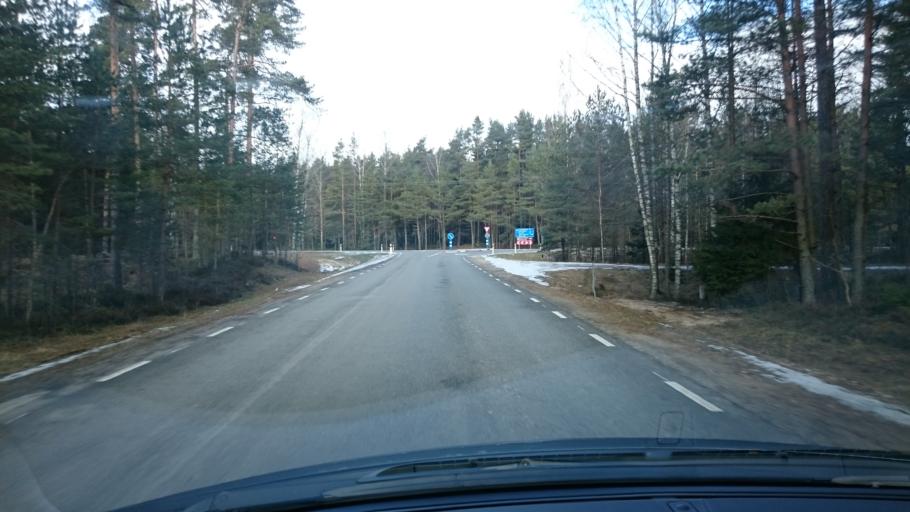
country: EE
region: Harju
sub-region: Keila linn
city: Keila
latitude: 59.3921
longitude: 24.2941
